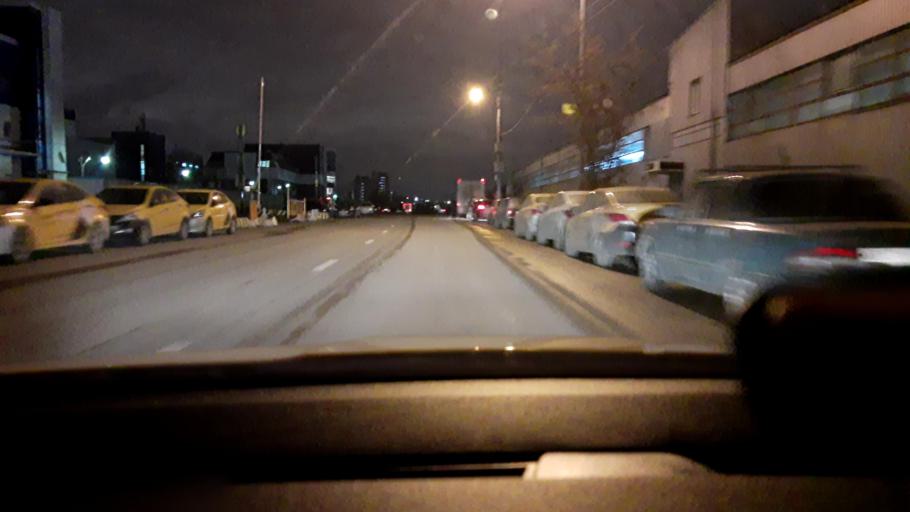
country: RU
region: Moscow
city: Mikhalkovo
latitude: 55.6929
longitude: 37.4187
